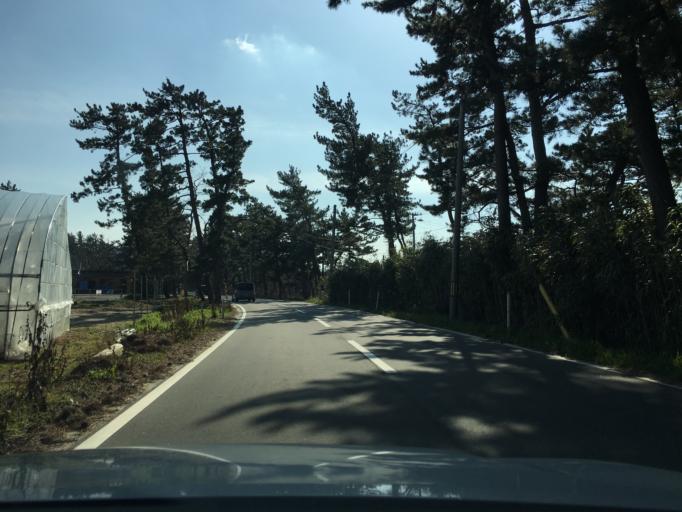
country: JP
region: Yamagata
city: Tsuruoka
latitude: 38.8001
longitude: 139.7718
